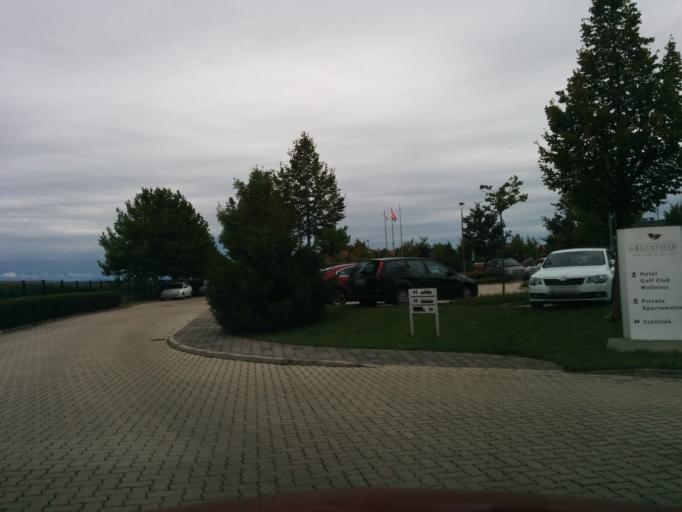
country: HU
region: Vas
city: Buk
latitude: 47.3881
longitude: 16.7812
